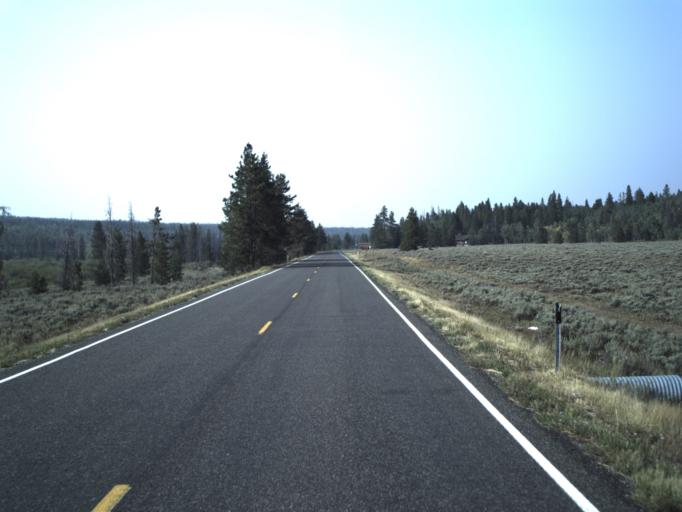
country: US
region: Wyoming
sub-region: Uinta County
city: Evanston
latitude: 40.8808
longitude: -110.8315
